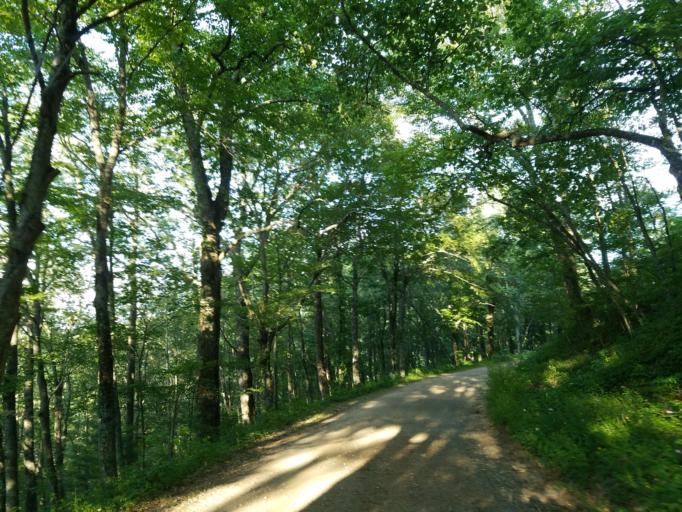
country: US
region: Georgia
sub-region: Lumpkin County
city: Dahlonega
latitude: 34.6570
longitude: -84.0902
